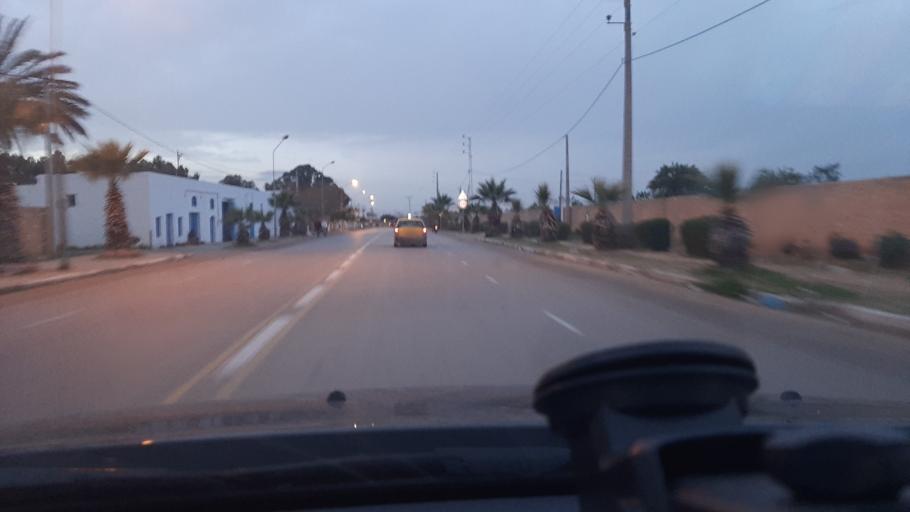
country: TN
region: Safaqis
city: Sfax
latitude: 34.7662
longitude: 10.6874
